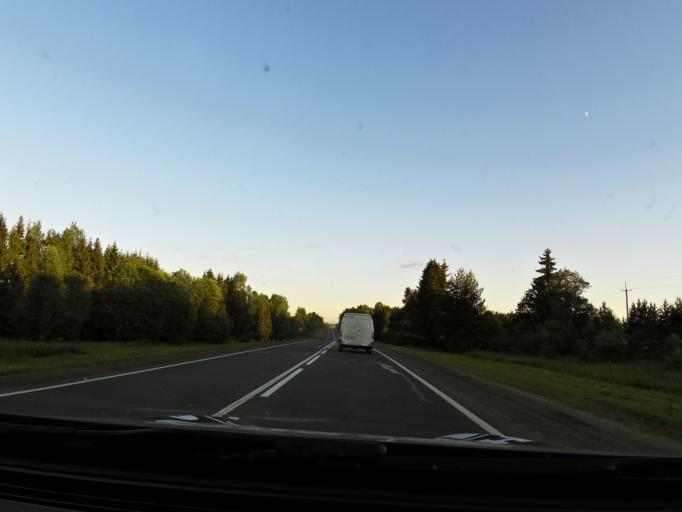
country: RU
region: Jaroslavl
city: Prechistoye
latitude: 58.4784
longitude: 40.3224
